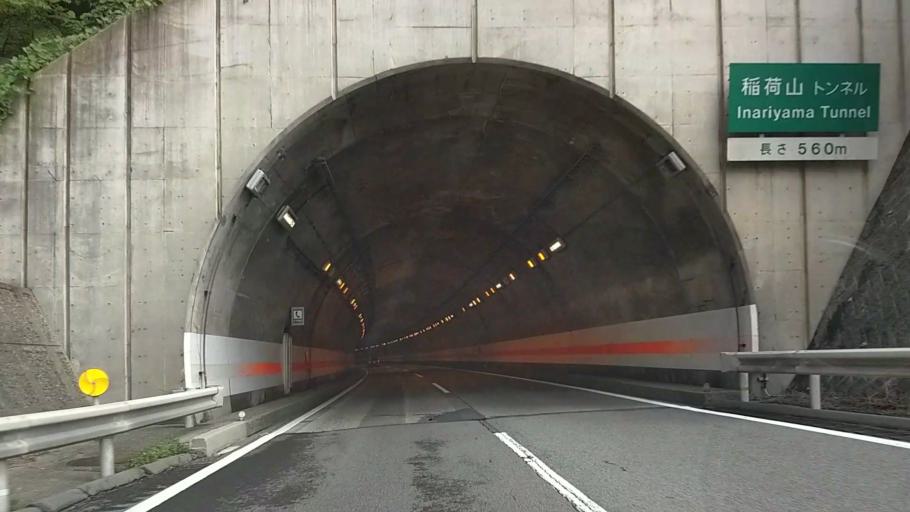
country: JP
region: Nagano
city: Nagano-shi
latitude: 36.5369
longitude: 138.0930
